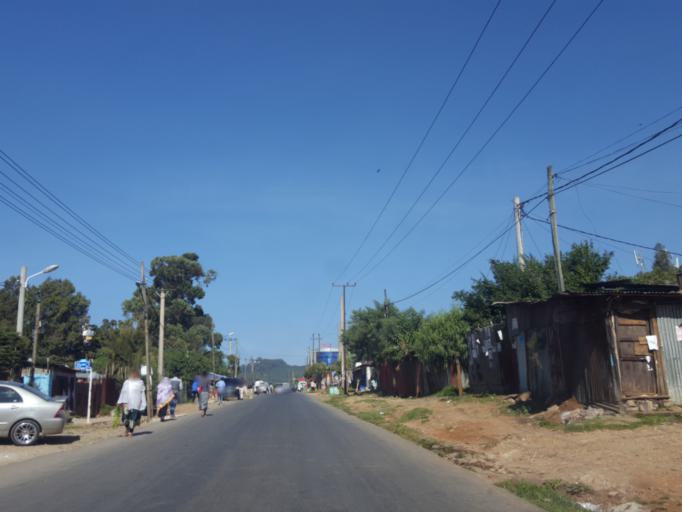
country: ET
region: Adis Abeba
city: Addis Ababa
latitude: 9.0575
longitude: 38.7293
